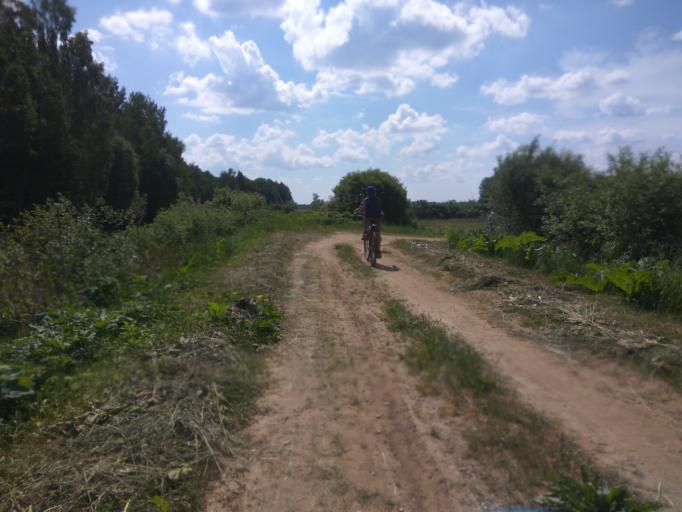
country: LV
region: Kuldigas Rajons
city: Kuldiga
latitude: 56.9308
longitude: 21.9758
